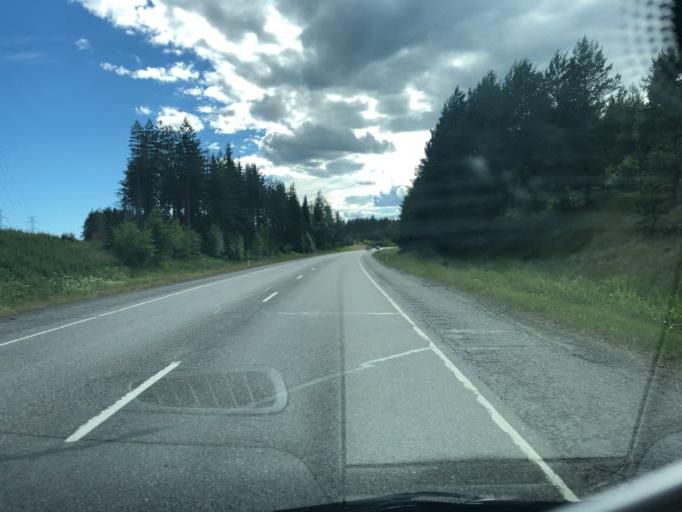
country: FI
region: Kymenlaakso
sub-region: Kouvola
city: Kouvola
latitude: 60.8681
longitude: 26.5858
